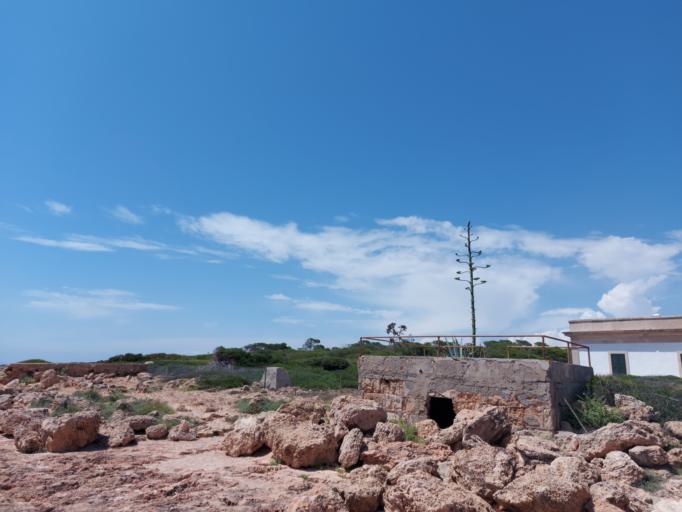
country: ES
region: Balearic Islands
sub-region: Illes Balears
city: Ses Salines
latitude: 39.2649
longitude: 3.0533
